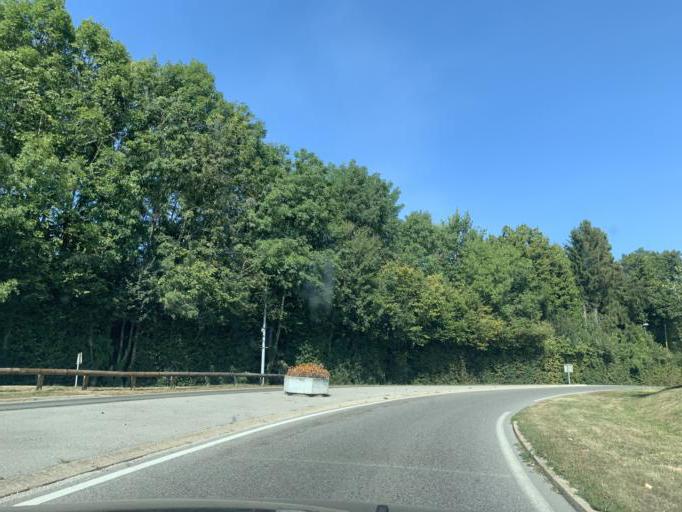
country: FR
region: Rhone-Alpes
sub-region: Departement de l'Ain
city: Chevry
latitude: 46.2831
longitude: 6.0385
